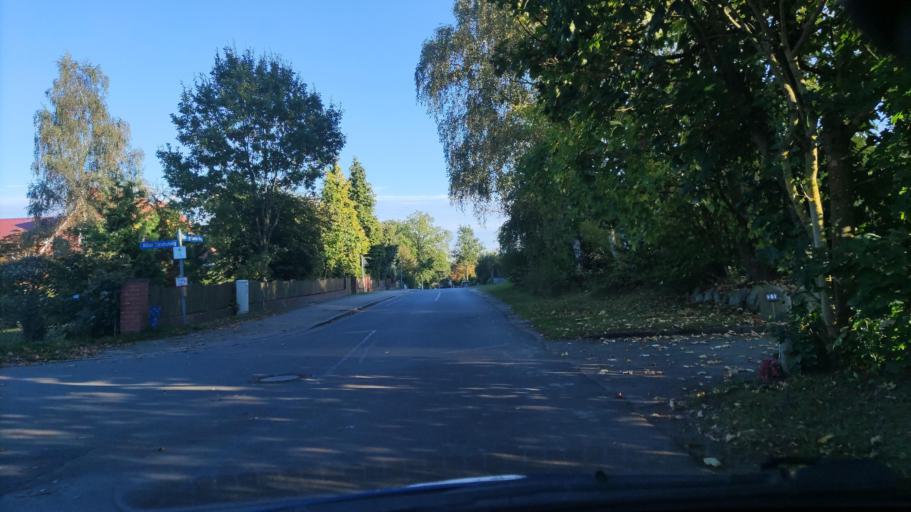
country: DE
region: Lower Saxony
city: Sudergellersen
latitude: 53.2103
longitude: 10.2922
